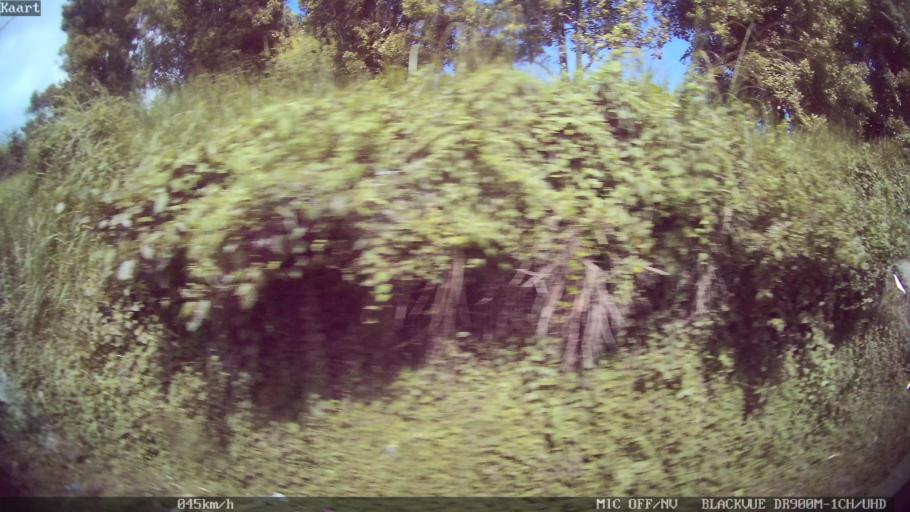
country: ID
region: Bali
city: Banjar Kelodan
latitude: -8.5229
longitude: 115.3295
